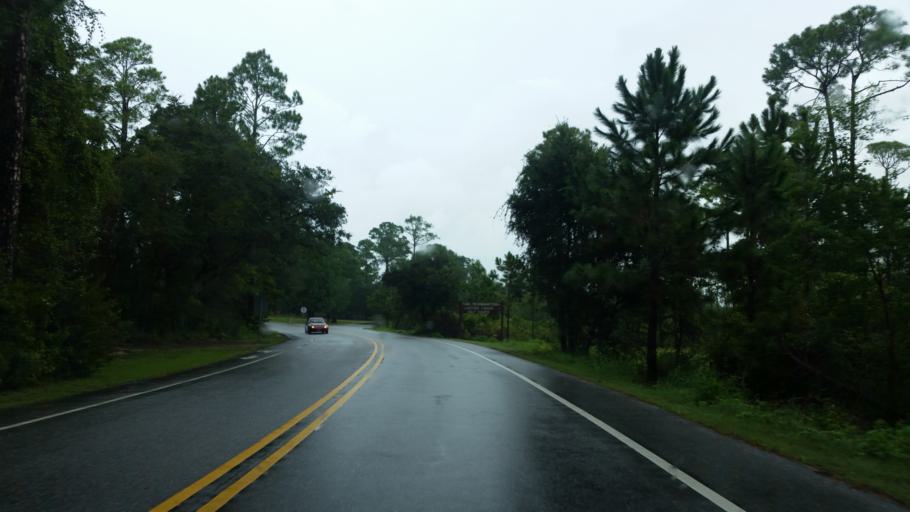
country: US
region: Alabama
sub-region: Baldwin County
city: Gulf Shores
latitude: 30.2642
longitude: -87.6774
